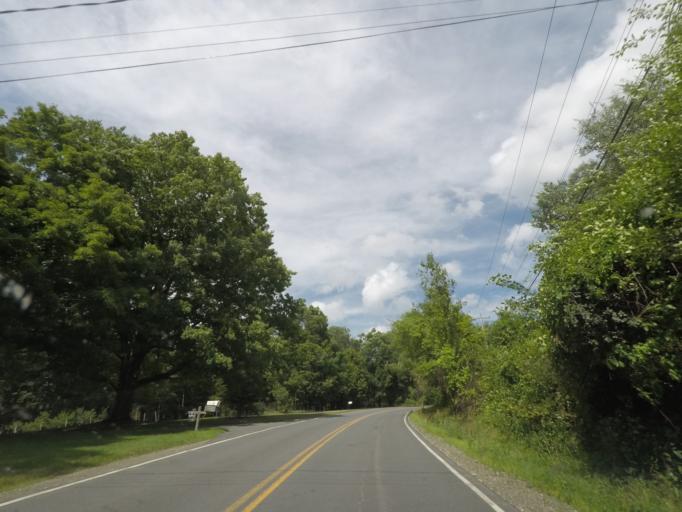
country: US
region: New York
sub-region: Rensselaer County
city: Wynantskill
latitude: 42.7198
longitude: -73.6279
